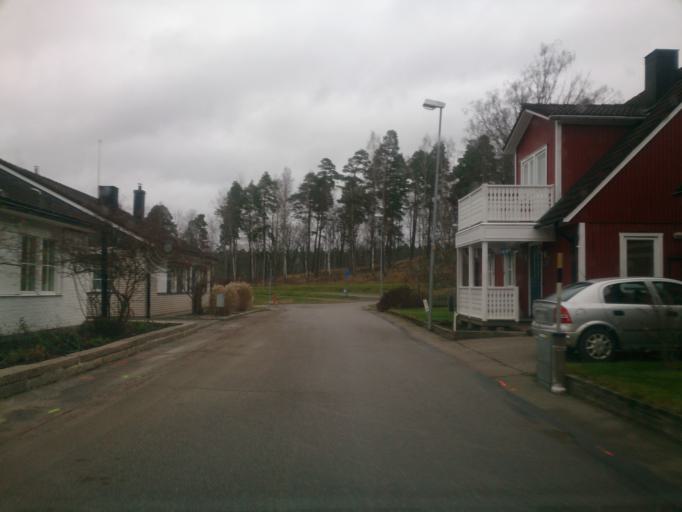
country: SE
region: OEstergoetland
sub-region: Atvidabergs Kommun
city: Atvidaberg
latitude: 58.2116
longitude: 15.9785
